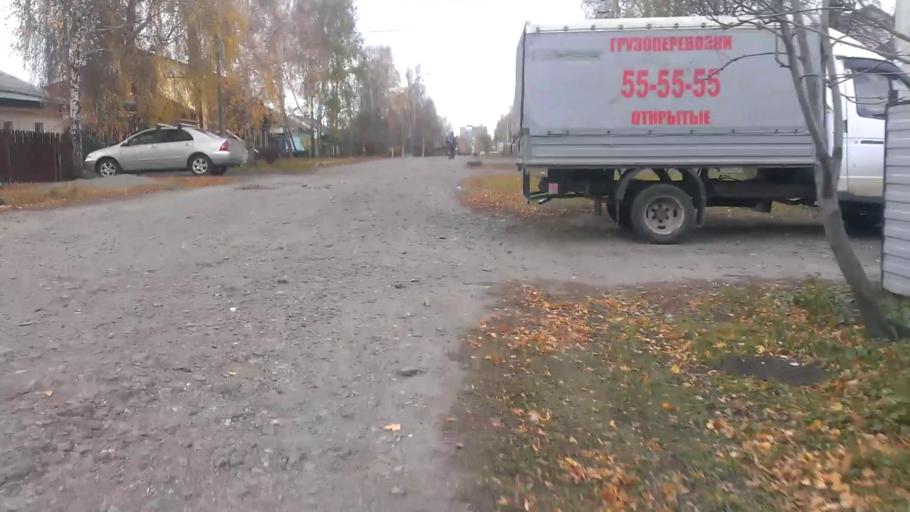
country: RU
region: Altai Krai
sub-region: Gorod Barnaulskiy
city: Barnaul
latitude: 53.3652
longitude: 83.7262
